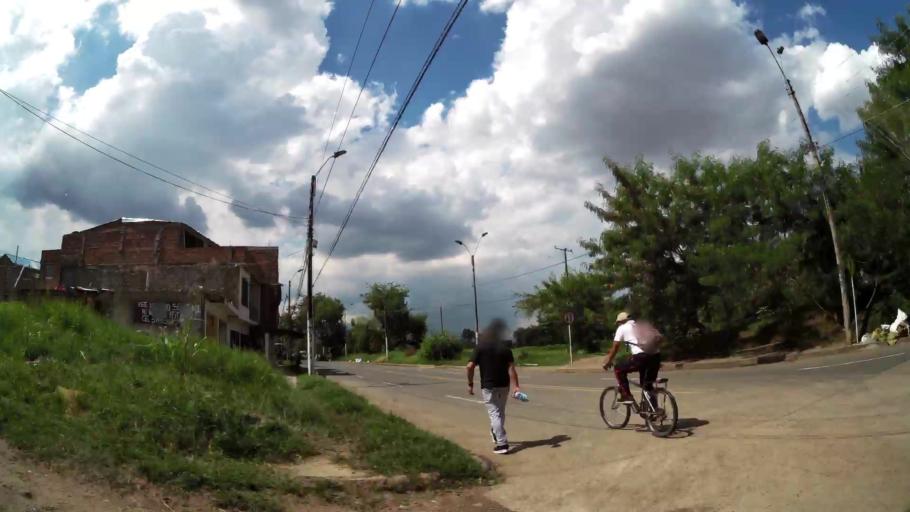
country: CO
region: Valle del Cauca
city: Cali
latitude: 3.4008
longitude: -76.5206
